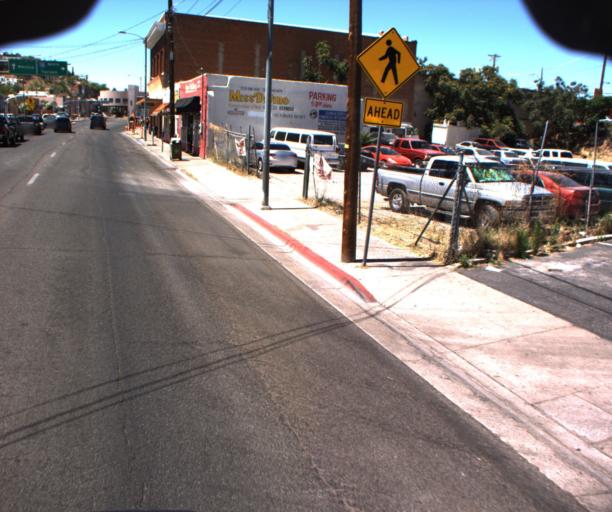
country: US
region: Arizona
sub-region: Santa Cruz County
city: Nogales
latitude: 31.3363
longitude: -110.9406
